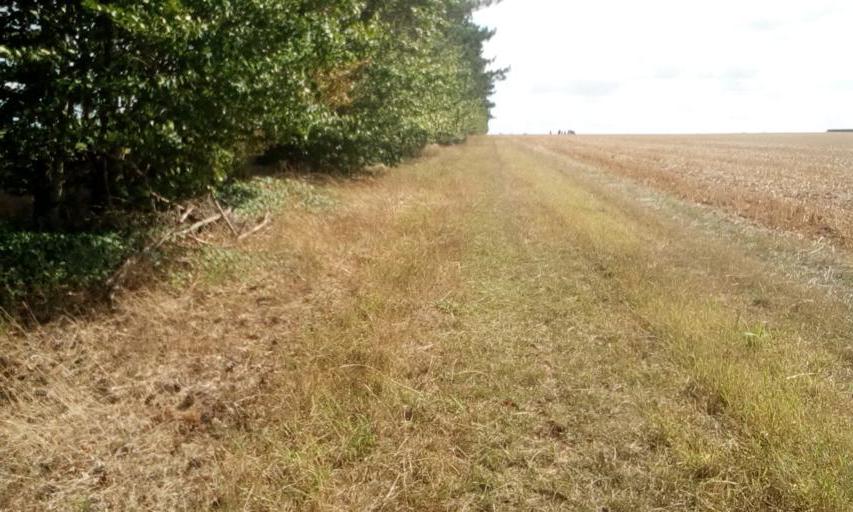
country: FR
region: Lower Normandy
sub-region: Departement du Calvados
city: Saint-Sylvain
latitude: 49.0808
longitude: -0.1981
